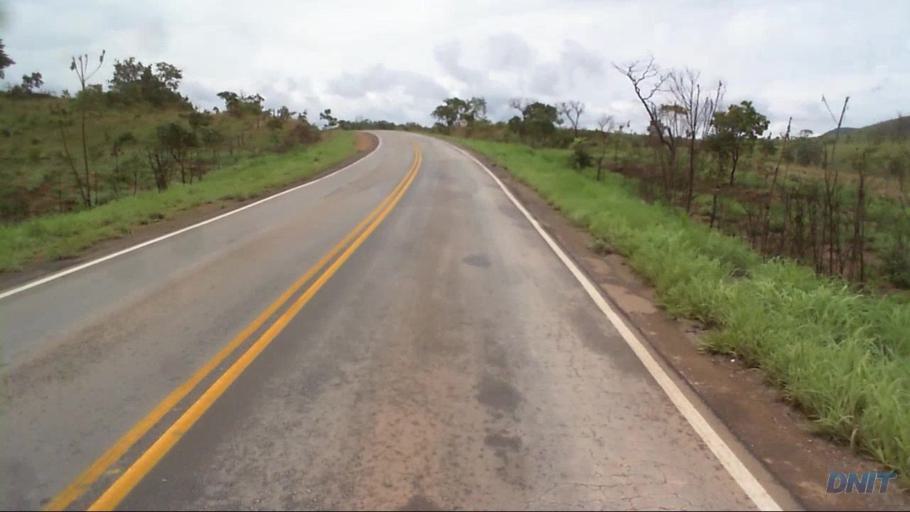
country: BR
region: Goias
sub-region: Padre Bernardo
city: Padre Bernardo
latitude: -15.4653
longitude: -48.2258
